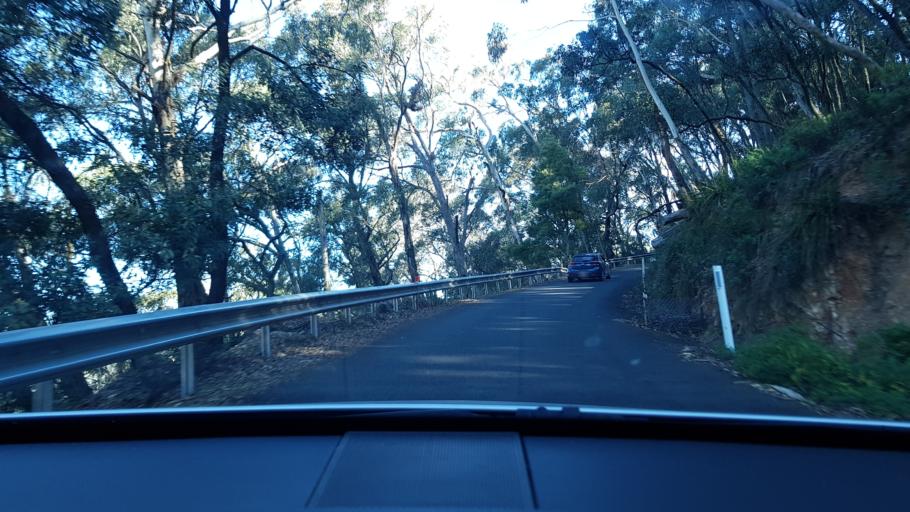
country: AU
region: New South Wales
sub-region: Oberon
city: Oberon
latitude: -33.8160
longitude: 150.0176
